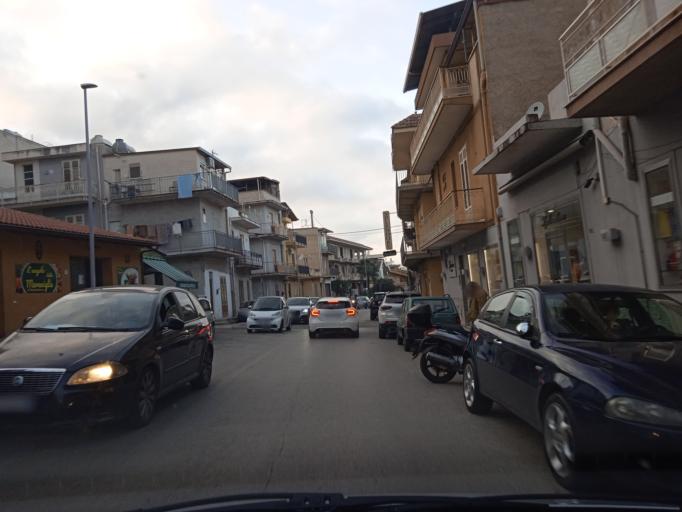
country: IT
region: Sicily
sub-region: Palermo
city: Villabate
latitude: 38.0762
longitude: 13.4401
